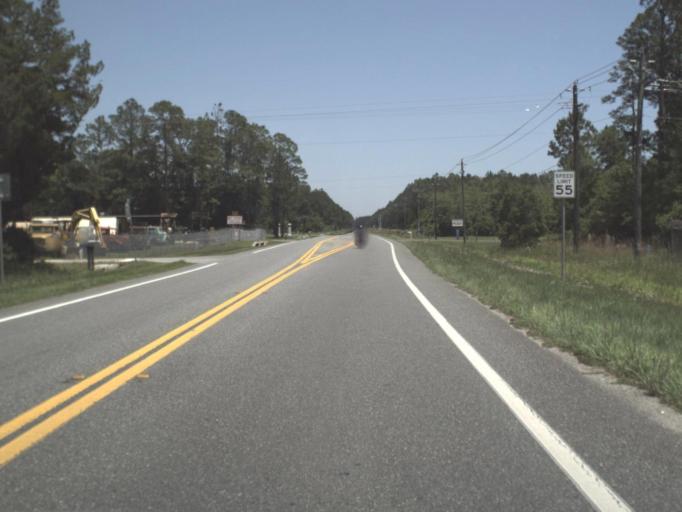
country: US
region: Florida
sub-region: Columbia County
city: Watertown
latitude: 30.1885
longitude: -82.5599
